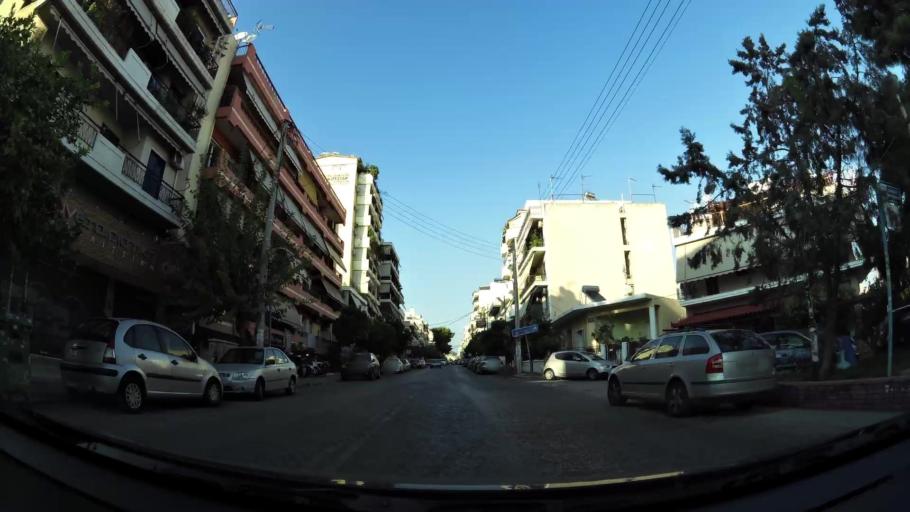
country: GR
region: Attica
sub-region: Nomos Piraios
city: Nikaia
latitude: 37.9690
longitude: 23.6381
